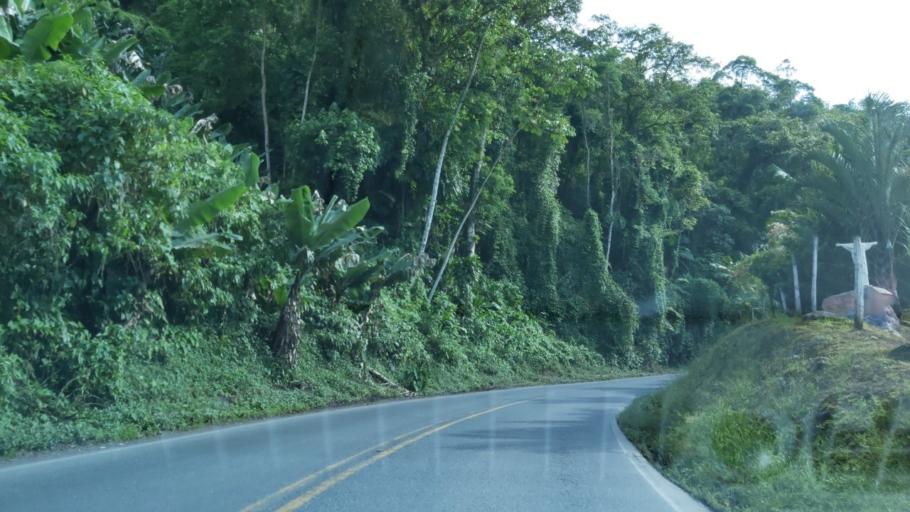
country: BR
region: Sao Paulo
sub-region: Juquia
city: Juquia
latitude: -24.0851
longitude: -47.6120
